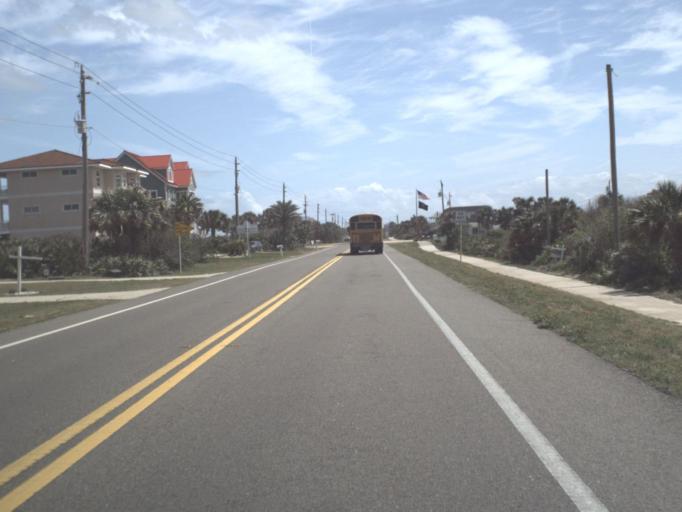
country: US
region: Florida
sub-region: Flagler County
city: Flagler Beach
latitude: 29.5291
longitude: -81.1517
